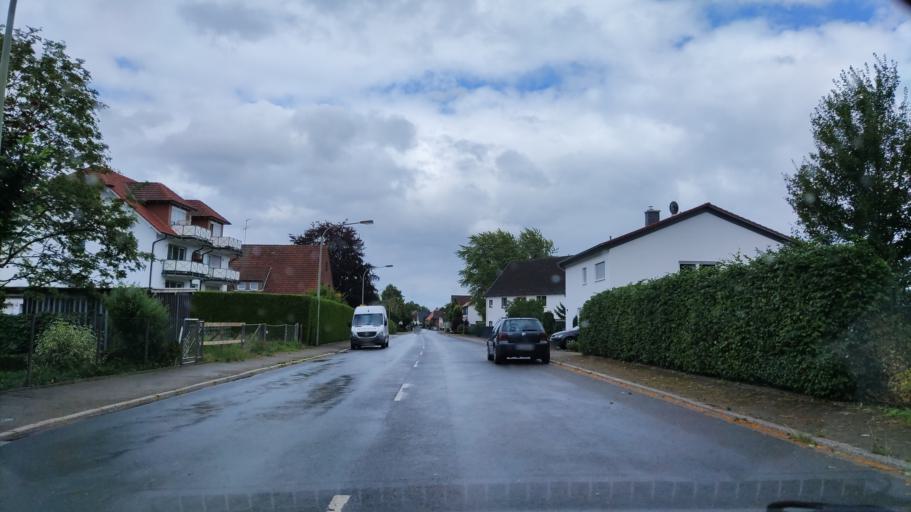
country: DE
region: North Rhine-Westphalia
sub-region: Regierungsbezirk Arnsberg
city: Welver
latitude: 51.6429
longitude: 7.9574
